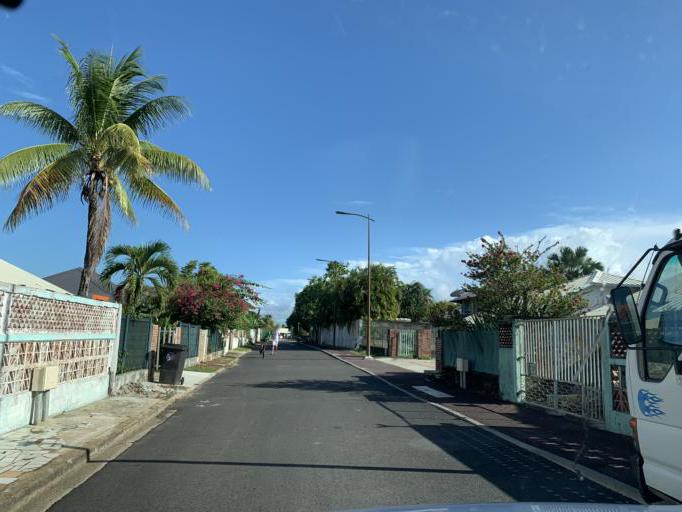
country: GF
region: Guyane
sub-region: Guyane
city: Kourou
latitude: 5.1740
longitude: -52.6467
